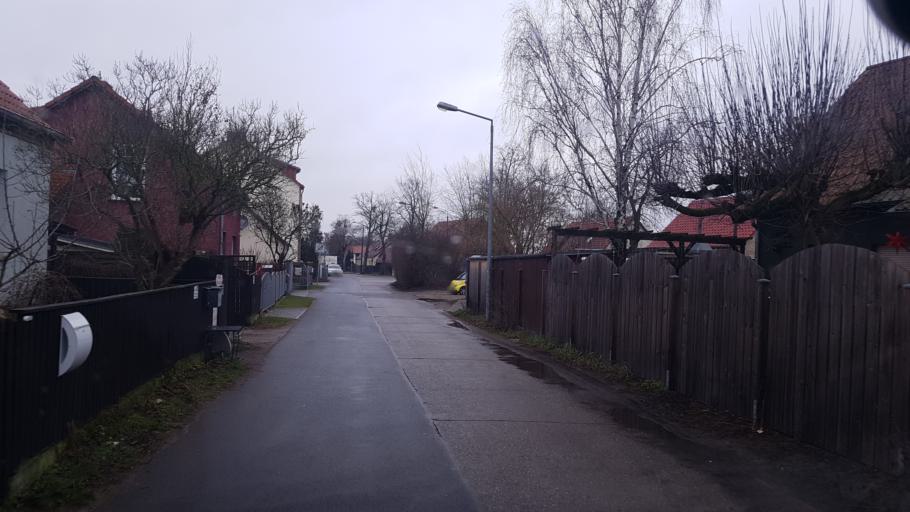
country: DE
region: Berlin
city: Wannsee
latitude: 52.3599
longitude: 13.1283
